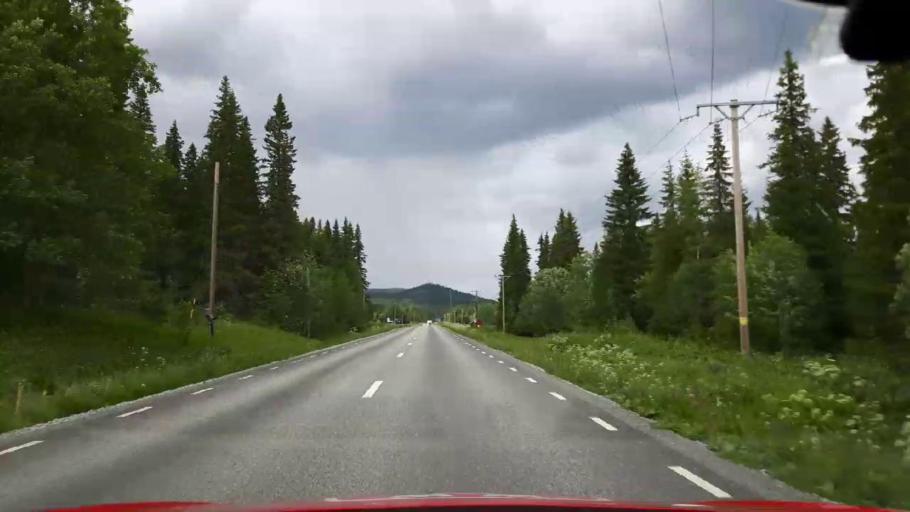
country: SE
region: Jaemtland
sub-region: Krokoms Kommun
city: Krokom
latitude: 63.6777
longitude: 14.3385
